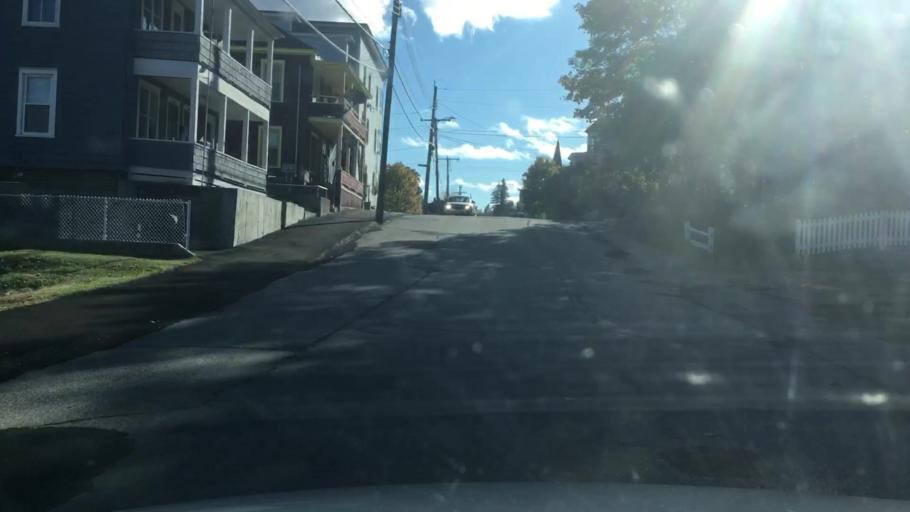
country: US
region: New Hampshire
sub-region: Coos County
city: Berlin
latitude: 44.4693
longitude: -71.1869
